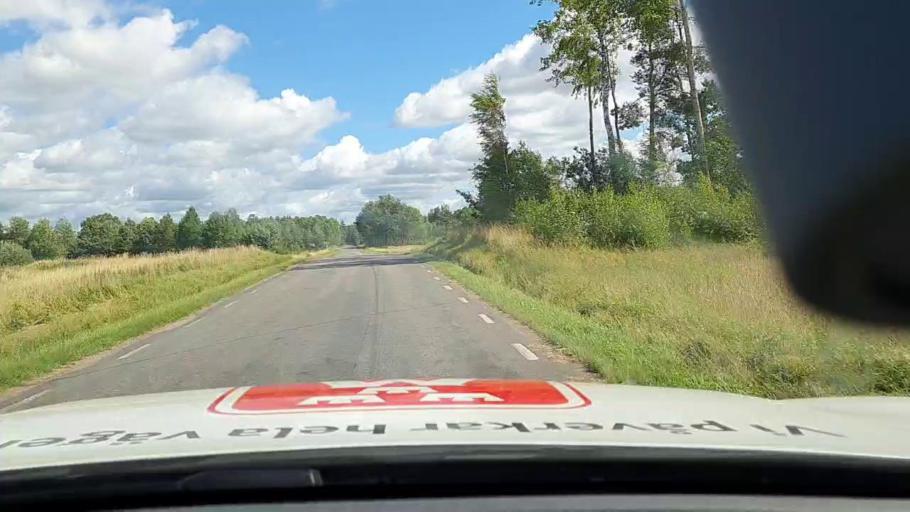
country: SE
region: Vaestra Goetaland
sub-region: Toreboda Kommun
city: Toereboda
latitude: 58.5699
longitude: 14.0320
